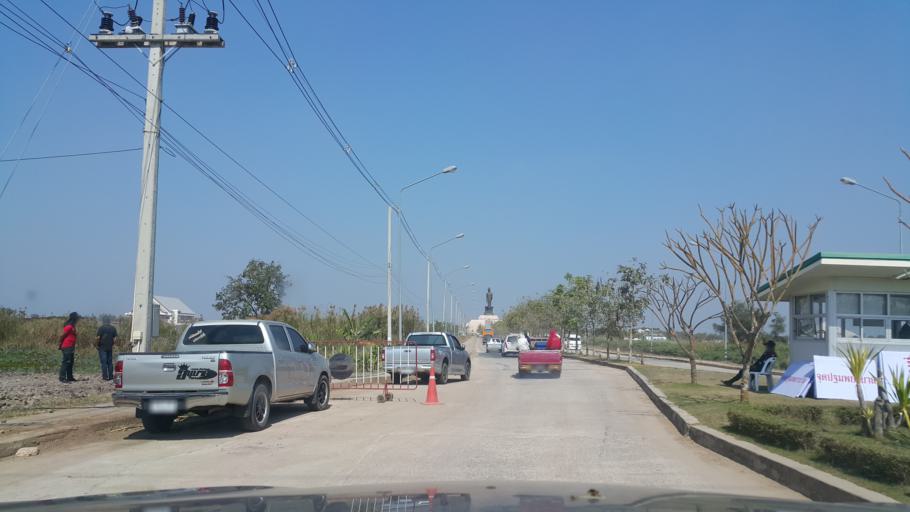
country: TH
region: Khon Kaen
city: Khon Kaen
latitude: 16.5076
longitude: 102.8664
